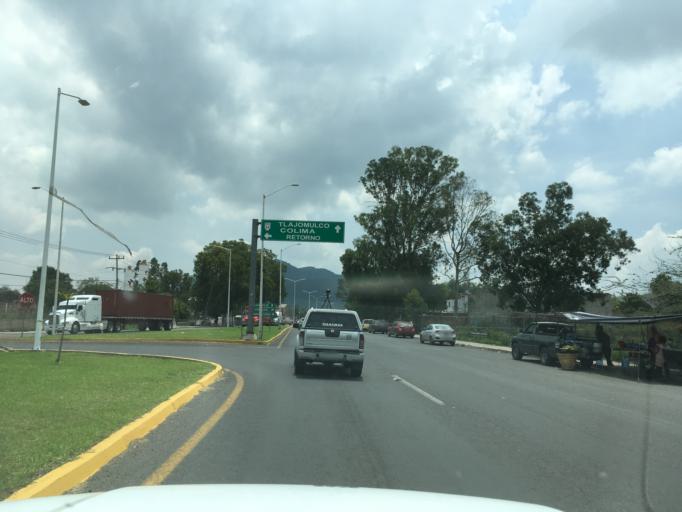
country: MX
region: Jalisco
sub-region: Tlajomulco de Zuniga
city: Santa Cruz de las Flores
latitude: 20.4885
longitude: -103.4961
